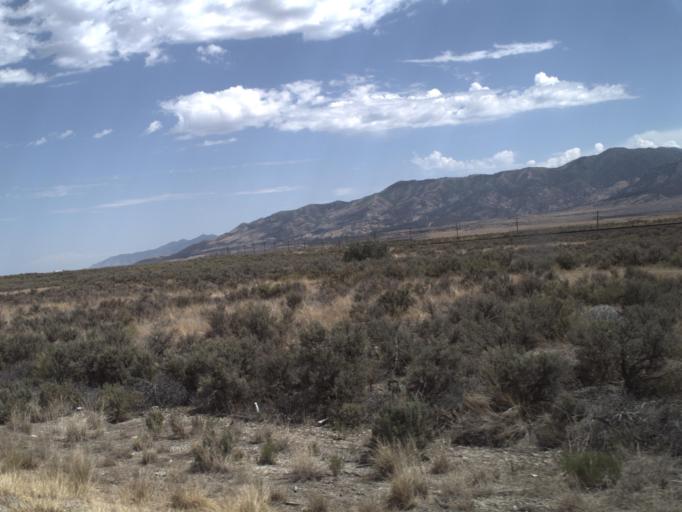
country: US
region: Utah
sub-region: Tooele County
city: Tooele
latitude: 40.3585
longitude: -112.4136
